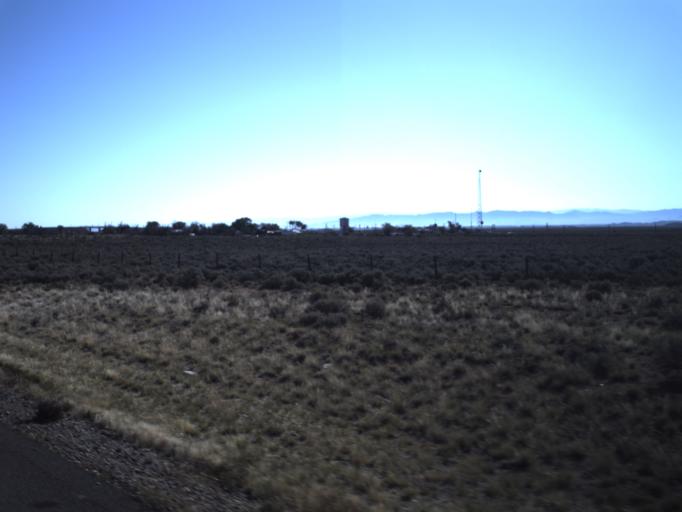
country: US
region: Utah
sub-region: Washington County
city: Enterprise
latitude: 37.7984
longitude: -113.9344
